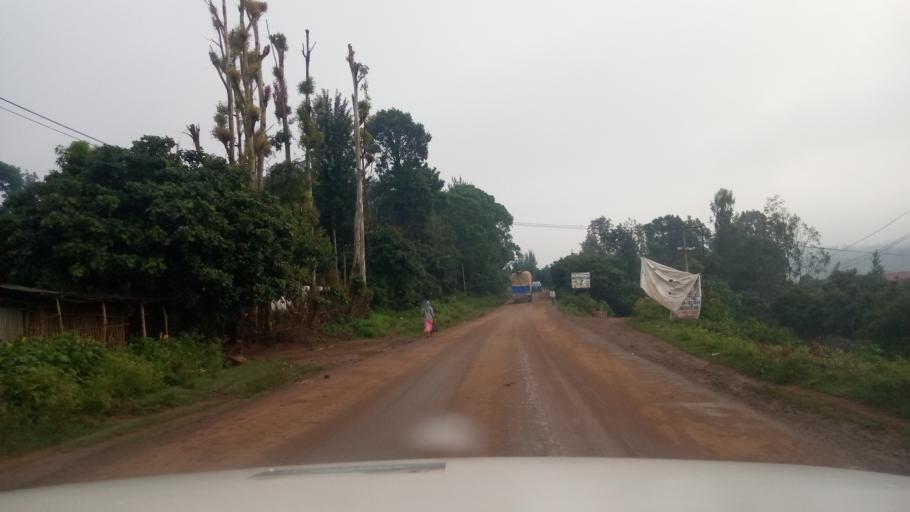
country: ET
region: Oromiya
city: Jima
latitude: 7.6893
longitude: 36.8262
